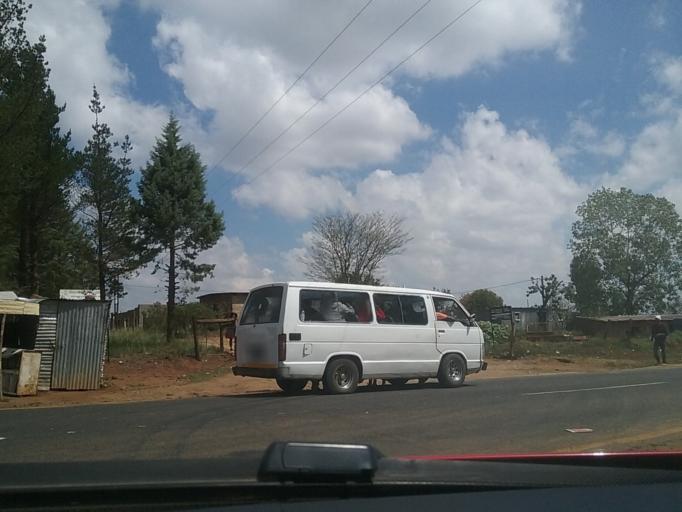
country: LS
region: Berea
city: Teyateyaneng
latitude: -29.2089
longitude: 27.8344
